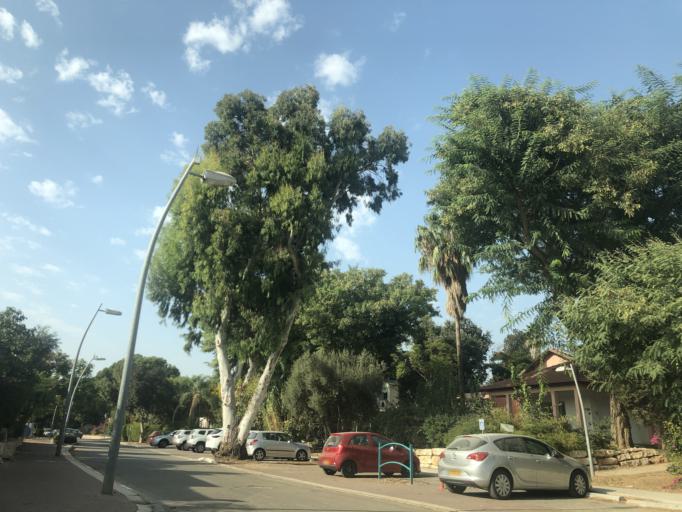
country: IL
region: Central District
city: Rosh Ha'Ayin
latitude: 32.0818
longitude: 34.9360
